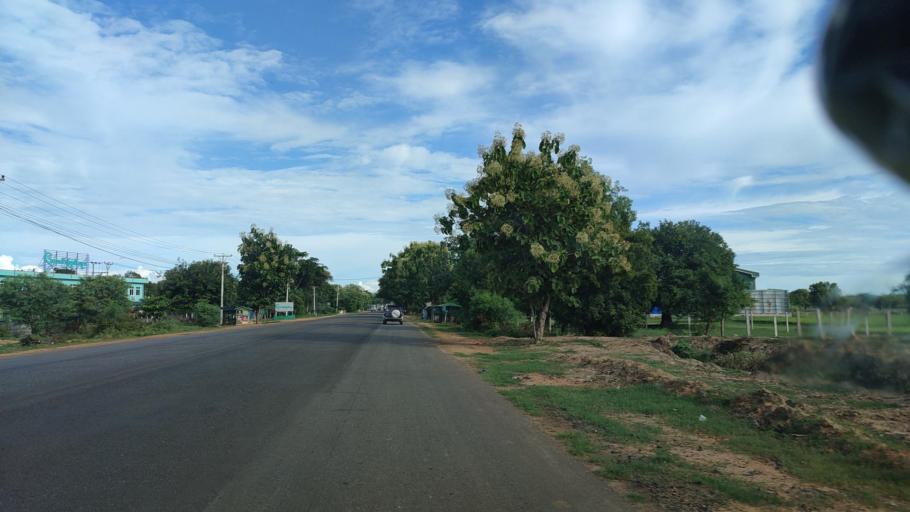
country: MM
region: Mandalay
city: Yamethin
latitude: 20.4494
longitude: 96.1294
